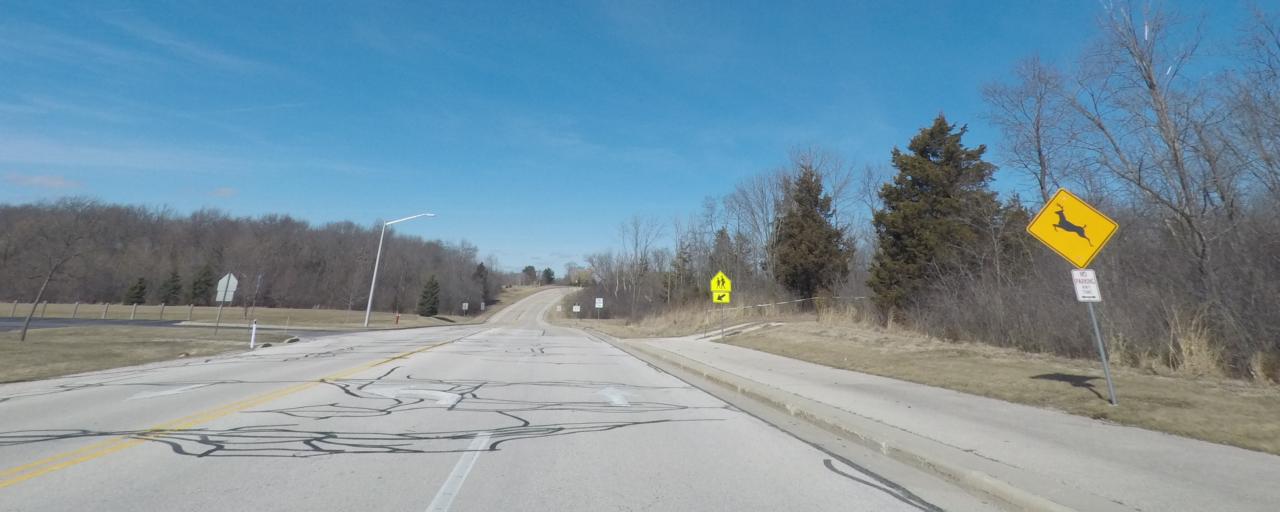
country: US
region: Wisconsin
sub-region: Waukesha County
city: Hartland
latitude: 43.1116
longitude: -88.3578
